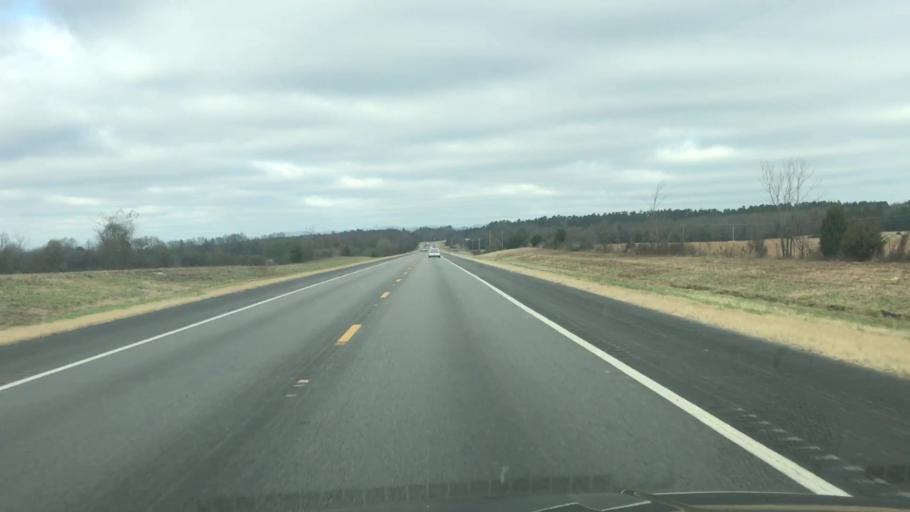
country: US
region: Arkansas
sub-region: Scott County
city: Waldron
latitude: 34.8757
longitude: -94.0925
